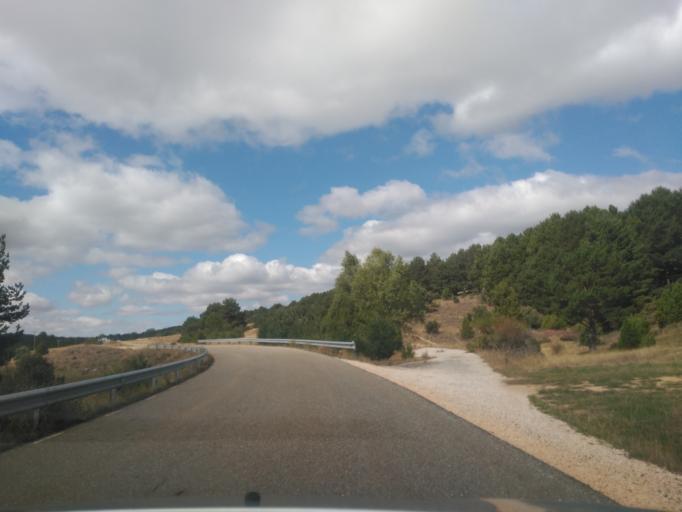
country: ES
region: Castille and Leon
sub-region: Provincia de Burgos
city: Rabanera del Pinar
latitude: 41.8544
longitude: -3.2103
